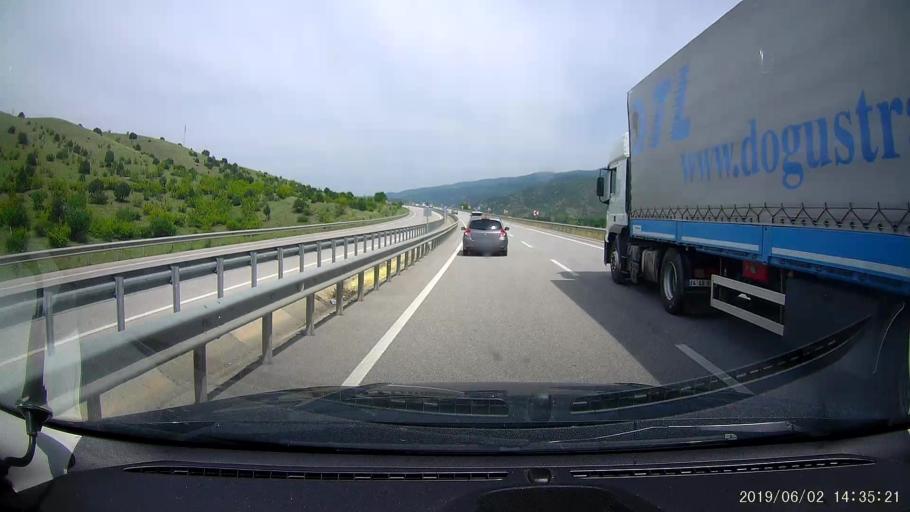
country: TR
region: Kastamonu
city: Tosya
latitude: 41.0402
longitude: 34.2131
